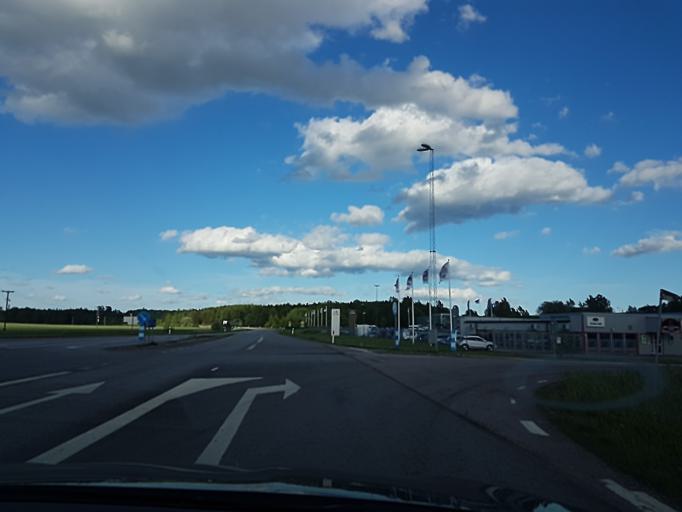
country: SE
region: Soedermanland
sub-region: Nykopings Kommun
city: Svalsta
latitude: 58.7430
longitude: 16.9156
